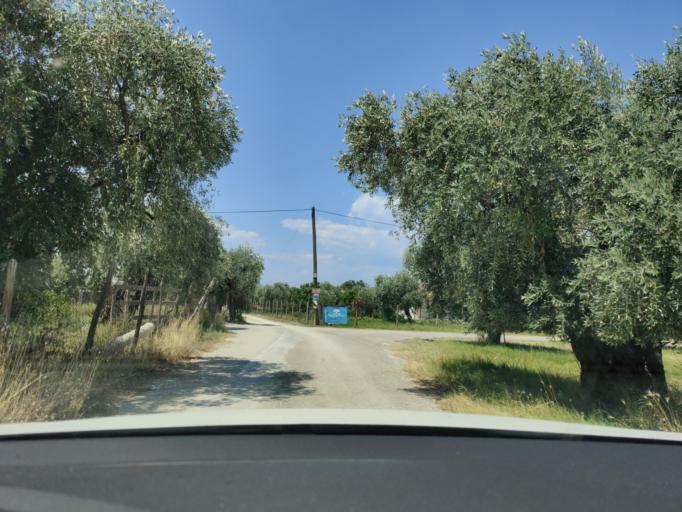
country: GR
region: East Macedonia and Thrace
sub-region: Nomos Kavalas
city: Prinos
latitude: 40.7693
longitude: 24.5970
